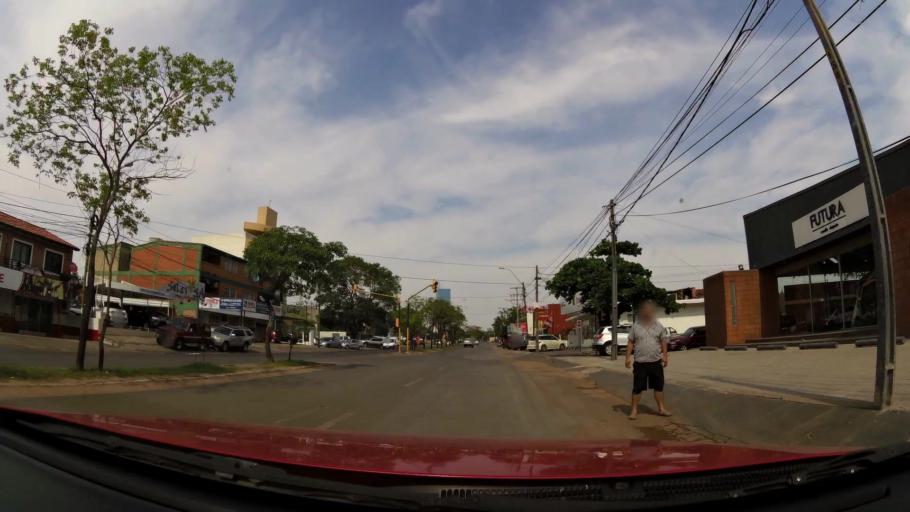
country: PY
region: Central
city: Fernando de la Mora
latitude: -25.2764
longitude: -57.5493
